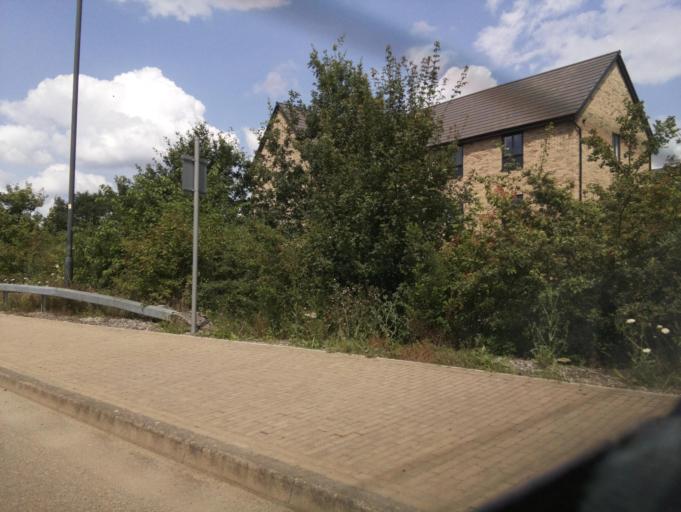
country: GB
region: England
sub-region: Borough of Swindon
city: Wroughton
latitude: 51.5451
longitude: -1.8066
